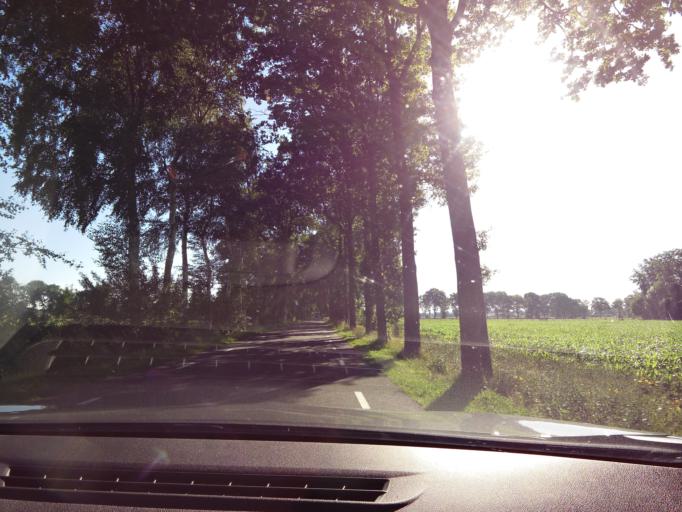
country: NL
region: Overijssel
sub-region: Gemeente Raalte
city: Raalte
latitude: 52.3076
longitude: 6.3259
